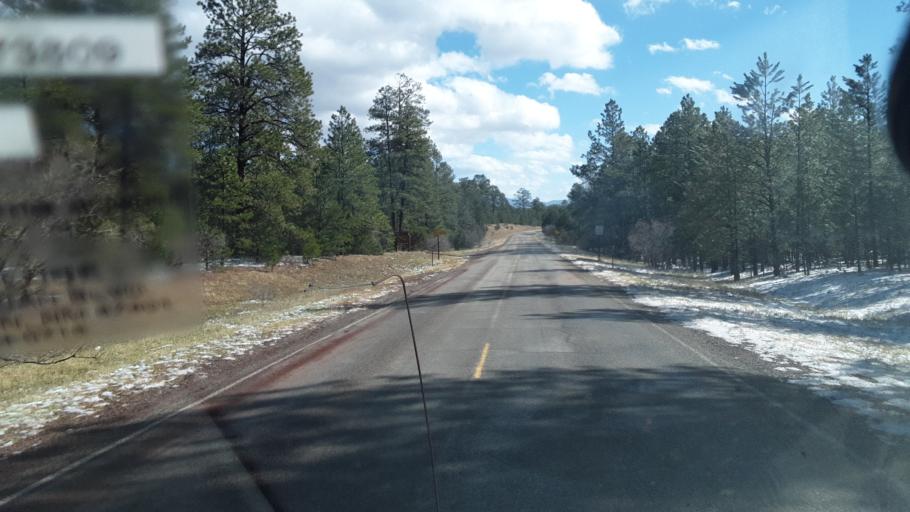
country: US
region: New Mexico
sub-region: Rio Arriba County
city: Santa Teresa
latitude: 36.1988
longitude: -106.7525
